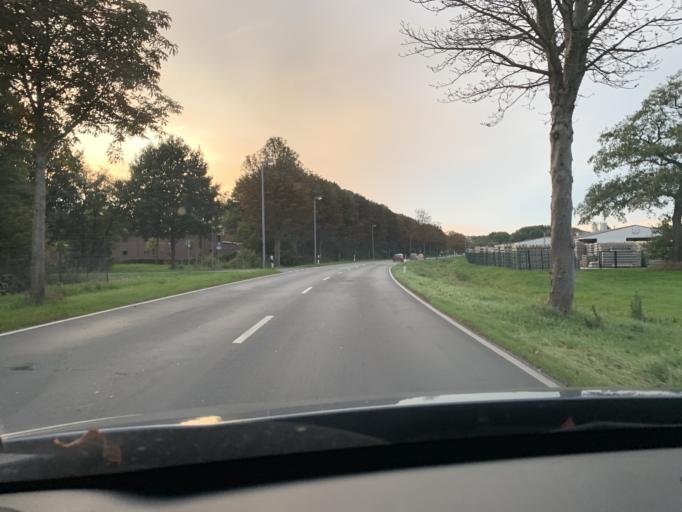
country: DE
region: Lower Saxony
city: Westerstede
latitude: 53.2497
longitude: 7.9203
